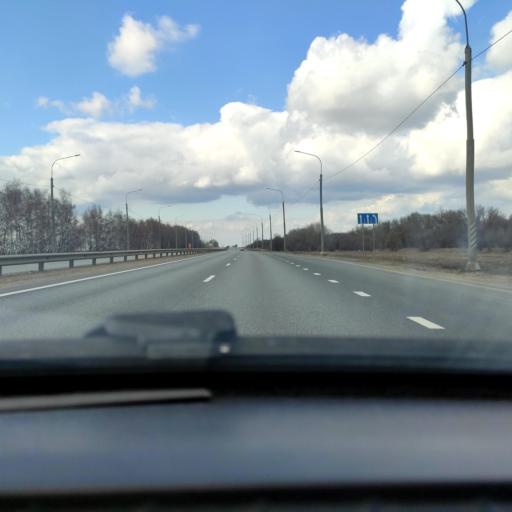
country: RU
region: Tula
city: Yefremov
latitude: 52.9921
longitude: 38.2295
